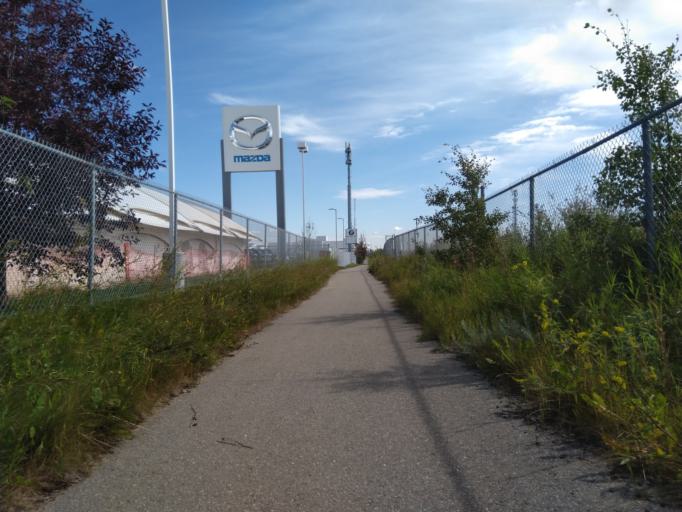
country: CA
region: Alberta
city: Calgary
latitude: 51.1514
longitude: -114.1965
